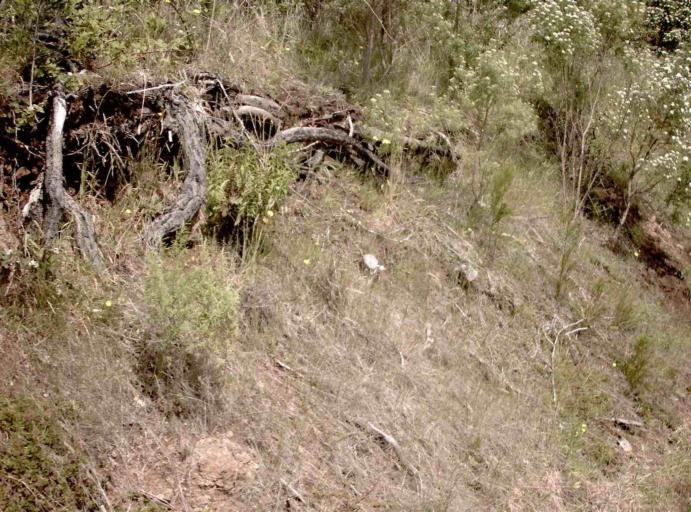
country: AU
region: Victoria
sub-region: Latrobe
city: Traralgon
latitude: -38.3420
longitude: 146.5722
